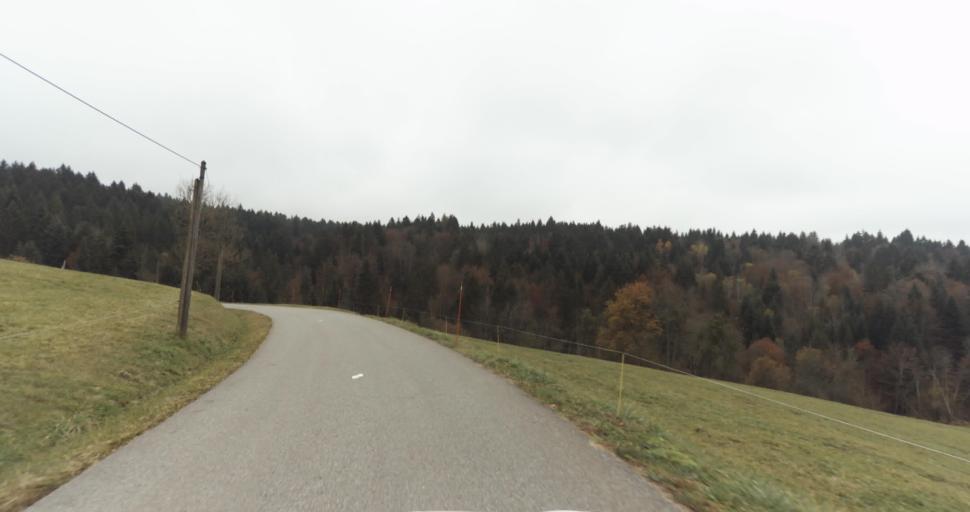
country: FR
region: Rhone-Alpes
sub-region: Departement de la Haute-Savoie
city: Saint-Jorioz
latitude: 45.7649
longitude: 6.1310
